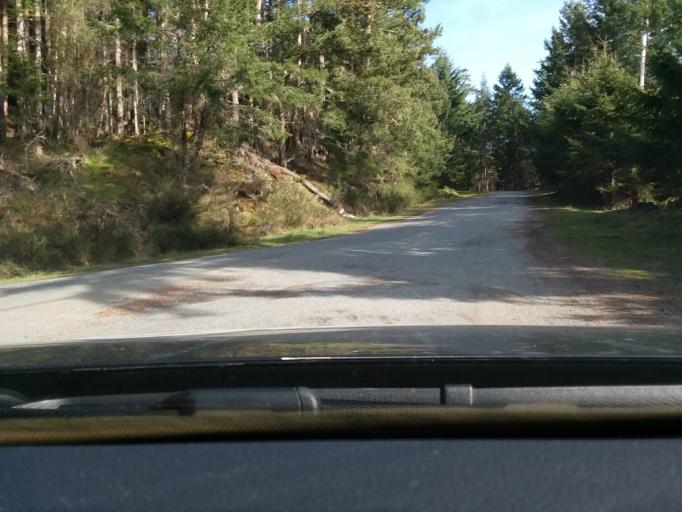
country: CA
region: British Columbia
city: North Saanich
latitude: 48.7692
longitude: -123.2930
